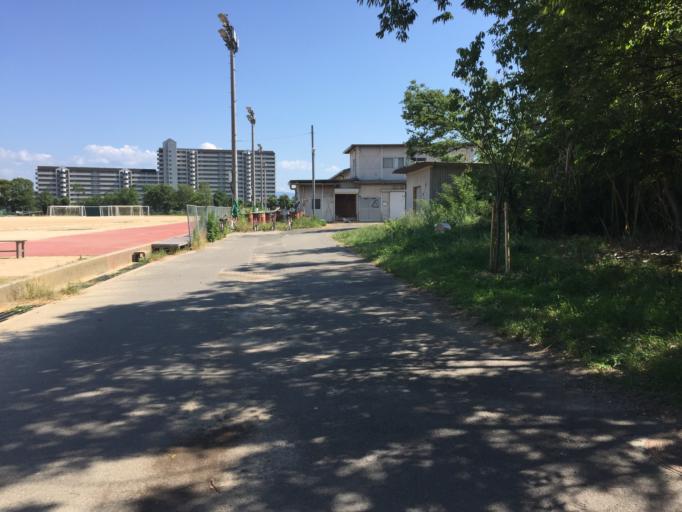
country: JP
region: Osaka
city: Sakai
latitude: 34.5893
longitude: 135.5031
